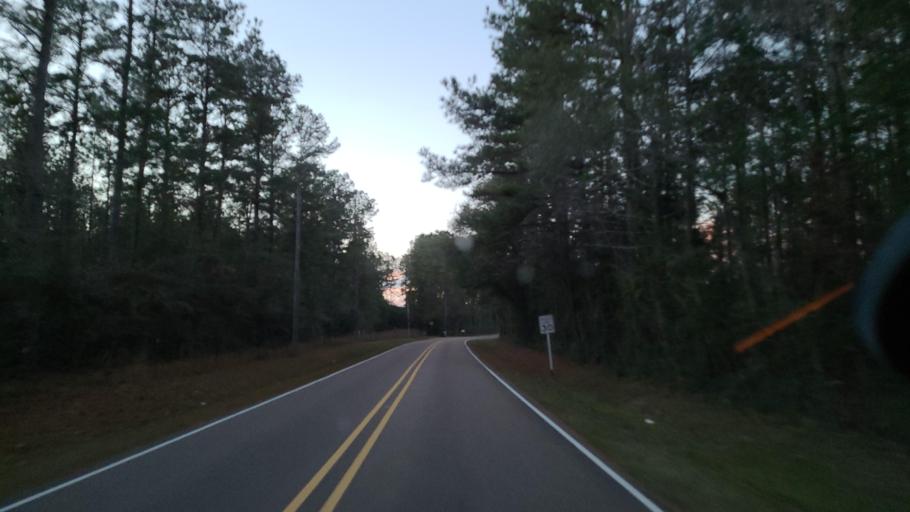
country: US
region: Mississippi
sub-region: Forrest County
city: Hattiesburg
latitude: 31.2318
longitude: -89.2399
